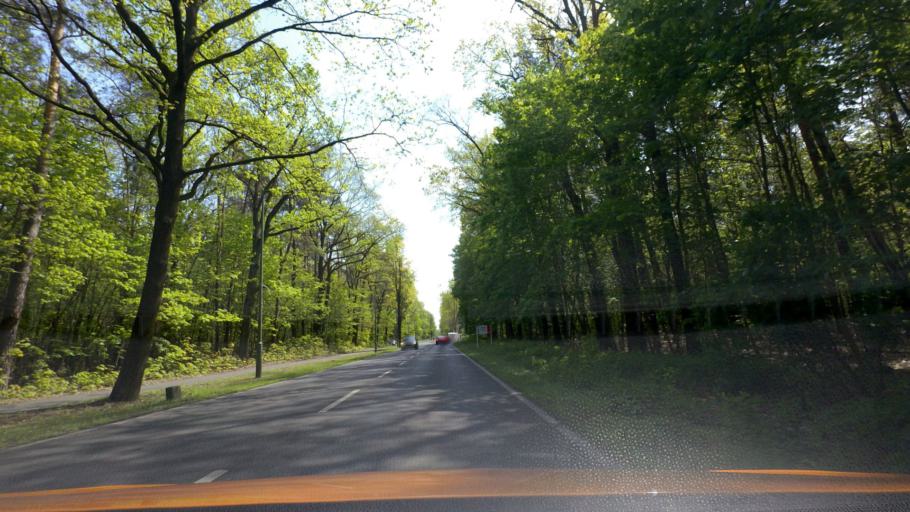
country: DE
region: Berlin
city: Grunau
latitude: 52.4062
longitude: 13.5876
